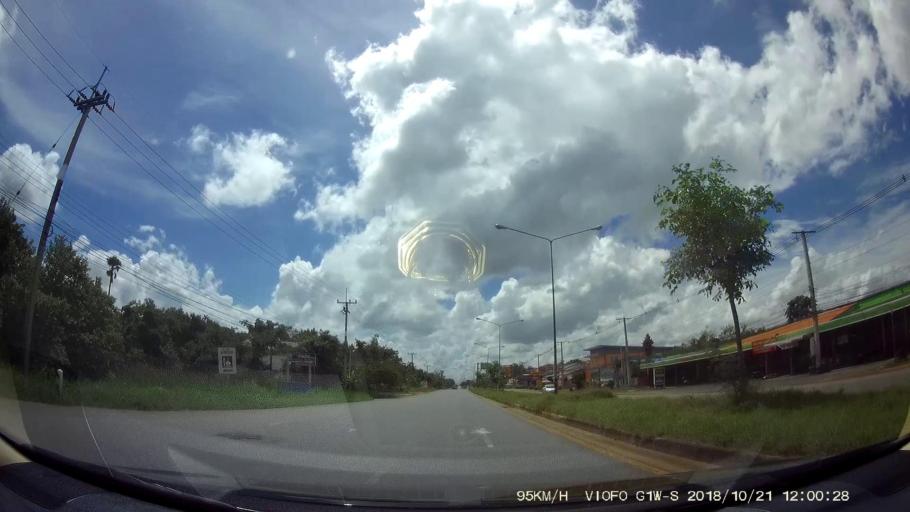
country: TH
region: Chaiyaphum
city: Chatturat
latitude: 15.5509
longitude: 101.8425
